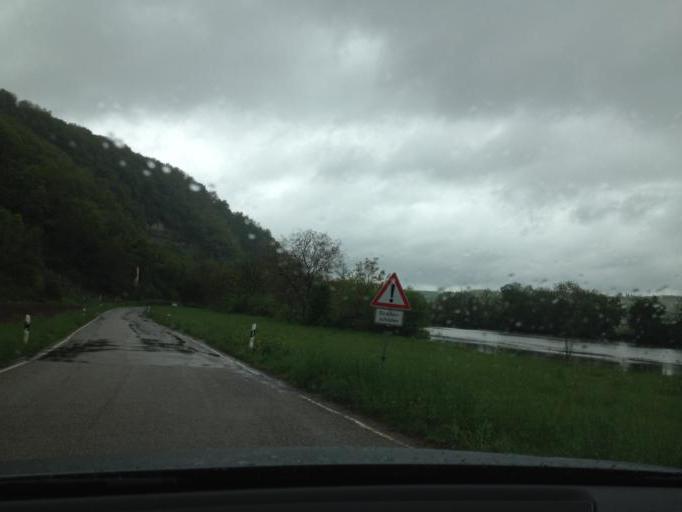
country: DE
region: Baden-Wuerttemberg
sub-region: Regierungsbezirk Stuttgart
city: Gundelsheim
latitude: 49.2684
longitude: 9.1490
